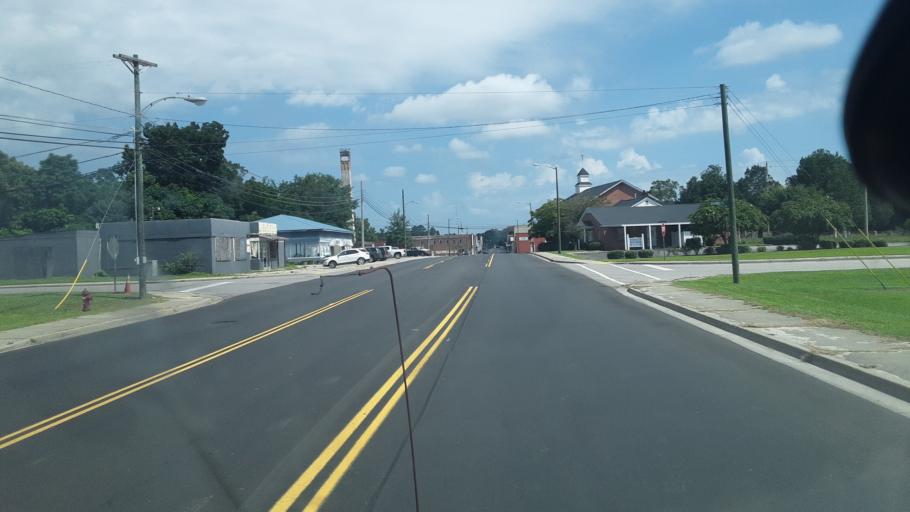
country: US
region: South Carolina
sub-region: Bamberg County
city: Bamberg
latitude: 33.2922
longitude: -81.0368
